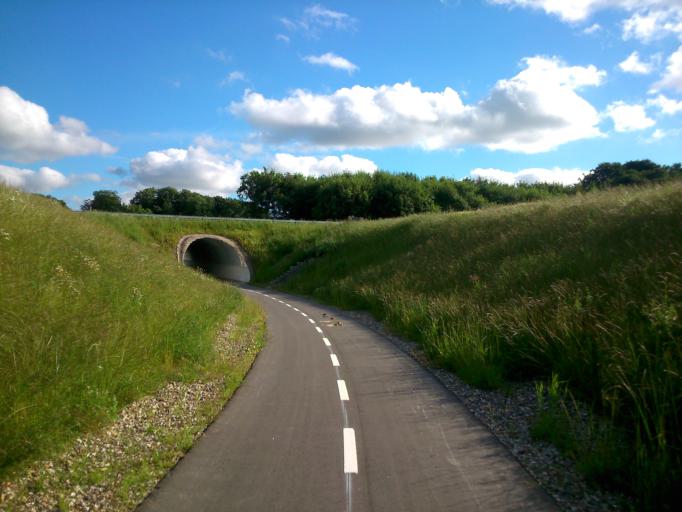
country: DK
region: Central Jutland
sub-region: Herning Kommune
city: Snejbjerg
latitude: 56.1853
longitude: 8.8437
